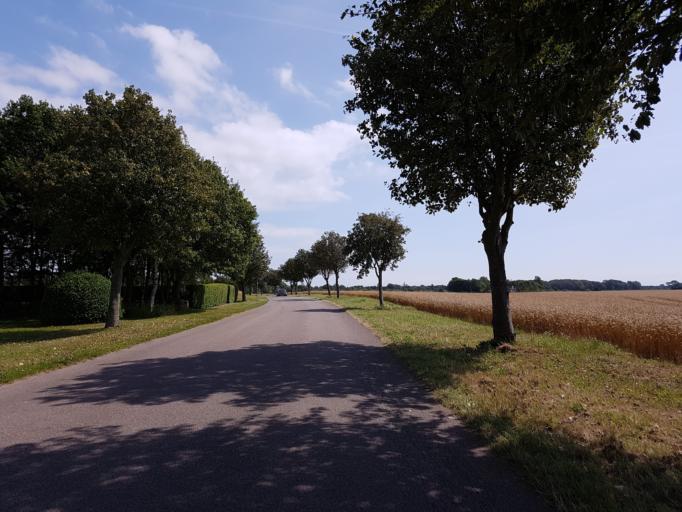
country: DK
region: Zealand
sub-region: Guldborgsund Kommune
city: Nykobing Falster
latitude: 54.6007
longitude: 11.9442
